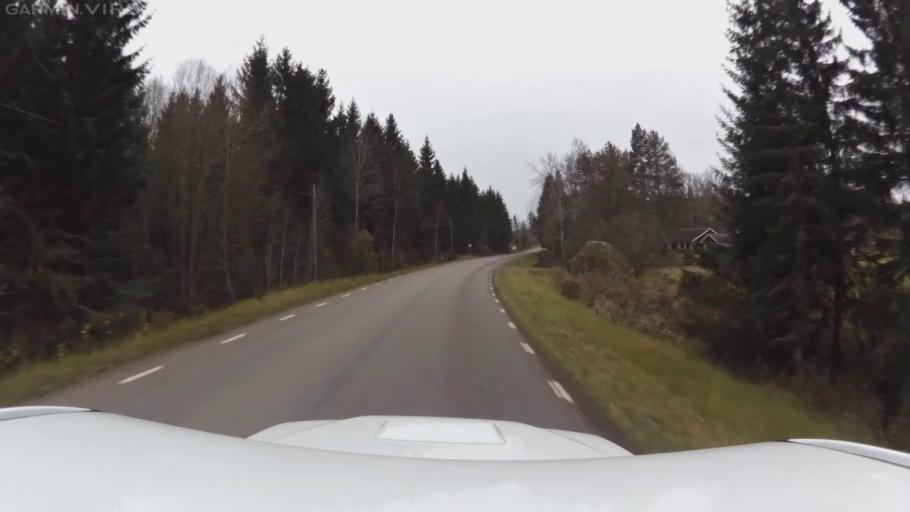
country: SE
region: OEstergoetland
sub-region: Linkopings Kommun
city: Vikingstad
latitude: 58.2505
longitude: 15.3862
